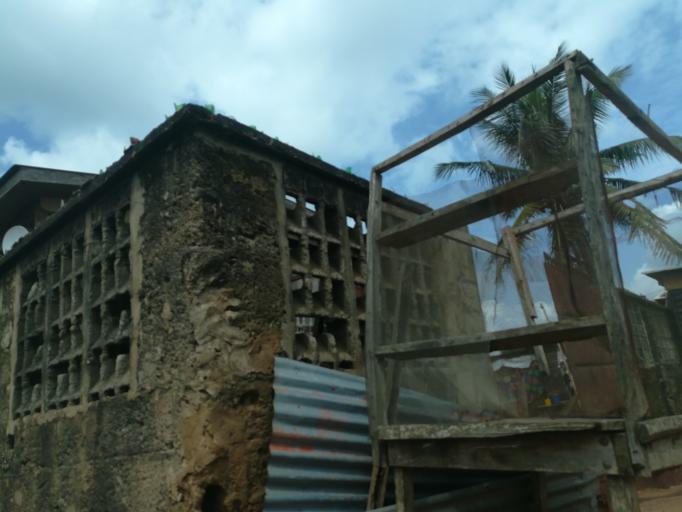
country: NG
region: Lagos
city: Ejirin
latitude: 6.6499
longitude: 3.7087
